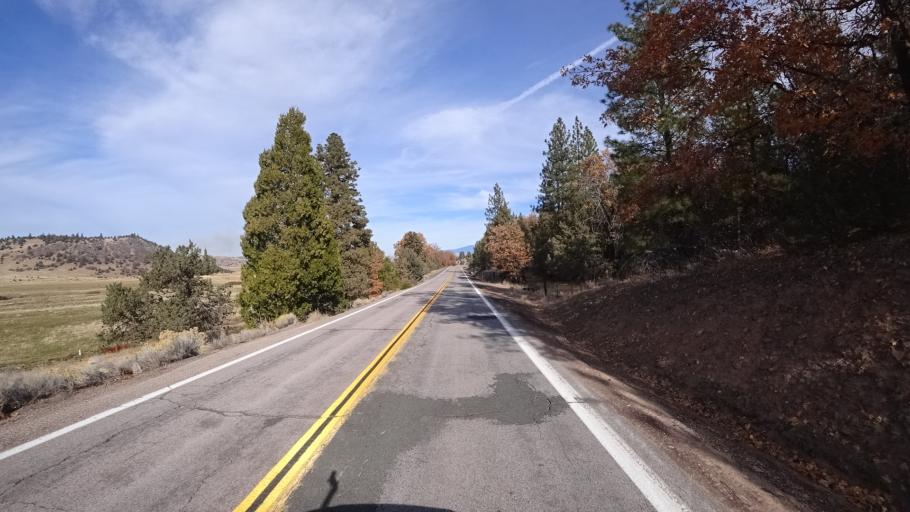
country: US
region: California
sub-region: Siskiyou County
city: Weed
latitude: 41.4728
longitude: -122.4135
